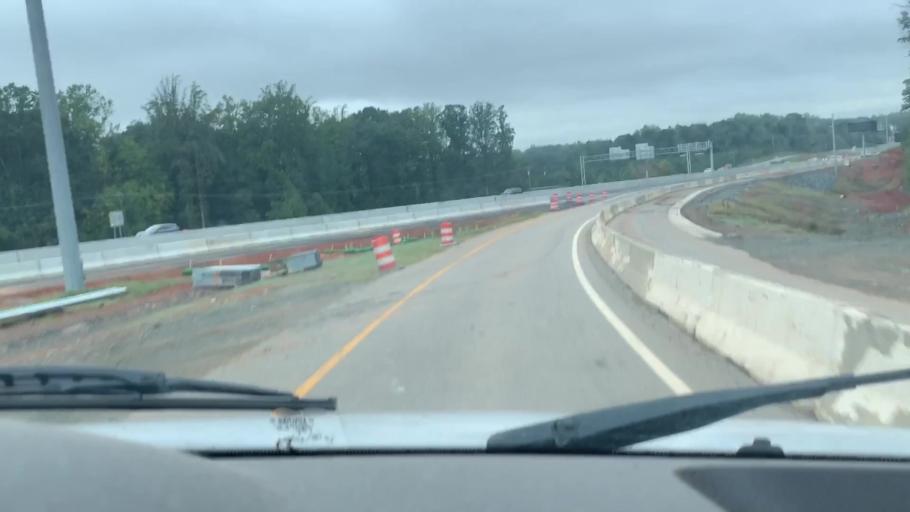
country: US
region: North Carolina
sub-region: Gaston County
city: Davidson
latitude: 35.5320
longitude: -80.8613
